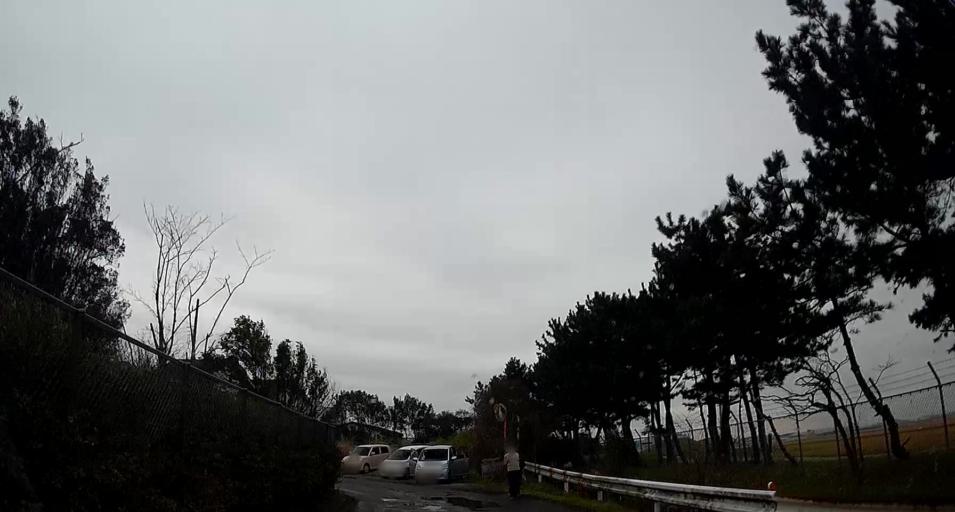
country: JP
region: Chiba
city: Kisarazu
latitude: 35.4050
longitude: 139.9143
